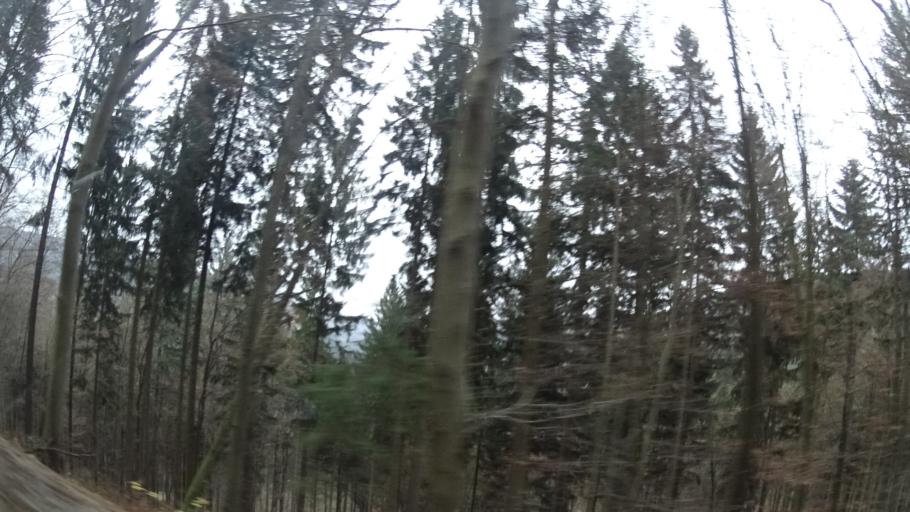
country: DE
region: Hesse
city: Hirschhorn
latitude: 49.4338
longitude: 8.9066
